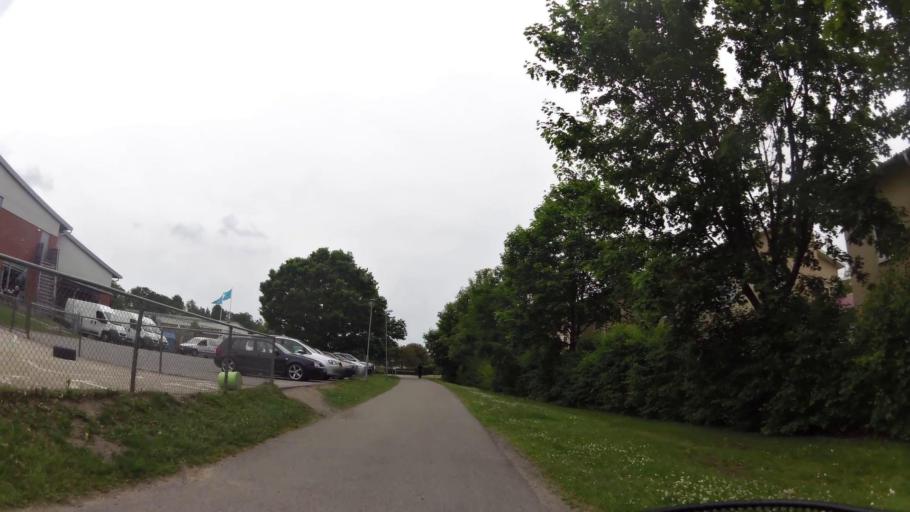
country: SE
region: OEstergoetland
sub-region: Linkopings Kommun
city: Malmslatt
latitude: 58.3869
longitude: 15.5656
